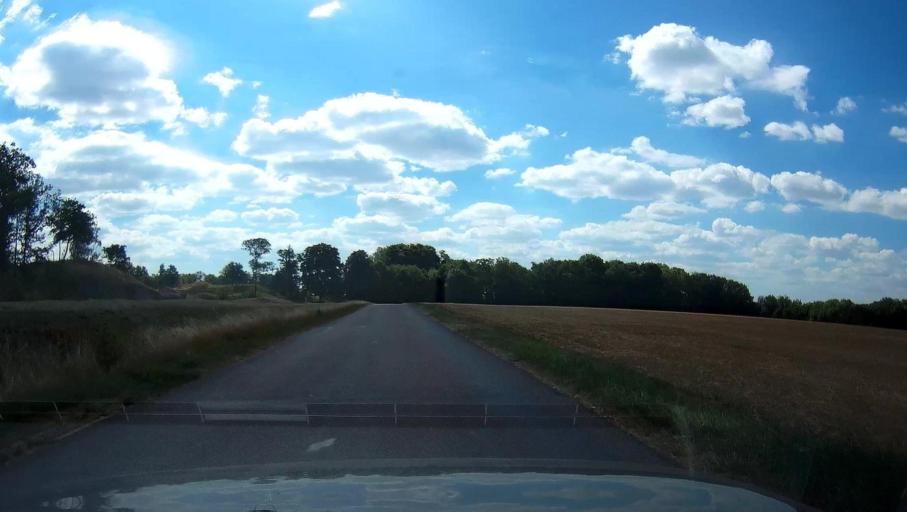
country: FR
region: Champagne-Ardenne
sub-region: Departement de la Haute-Marne
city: Langres
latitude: 47.8767
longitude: 5.3624
